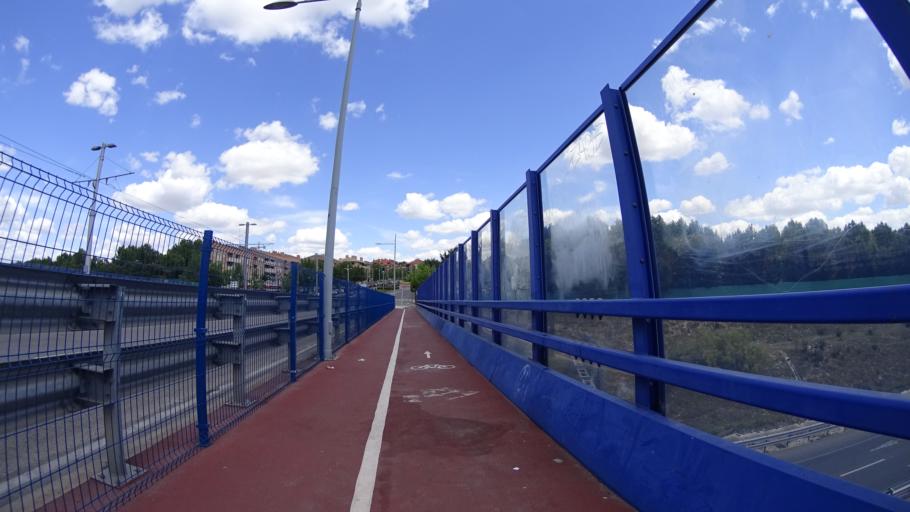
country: ES
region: Madrid
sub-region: Provincia de Madrid
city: Boadilla del Monte
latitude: 40.4054
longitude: -3.8906
